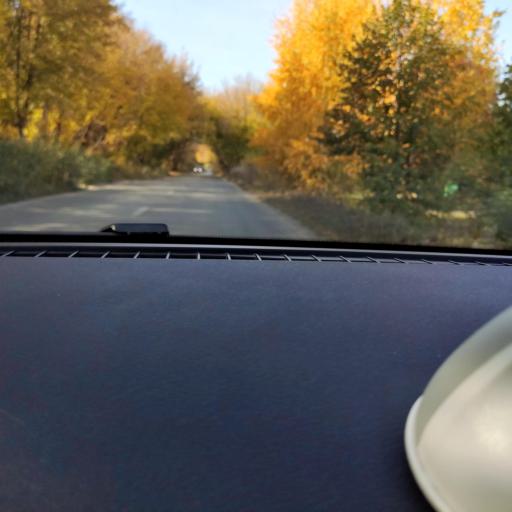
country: RU
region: Samara
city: Smyshlyayevka
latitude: 53.2398
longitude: 50.3472
